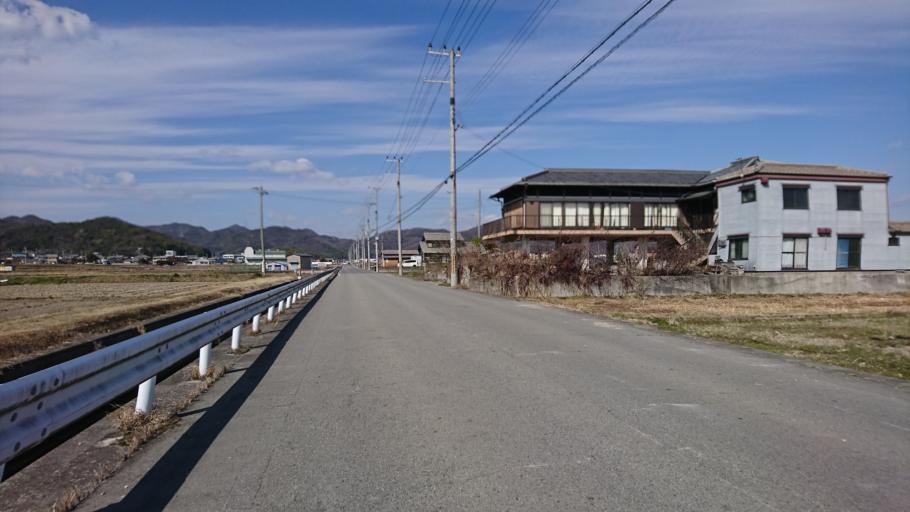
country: JP
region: Hyogo
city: Kakogawacho-honmachi
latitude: 34.8077
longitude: 134.8097
